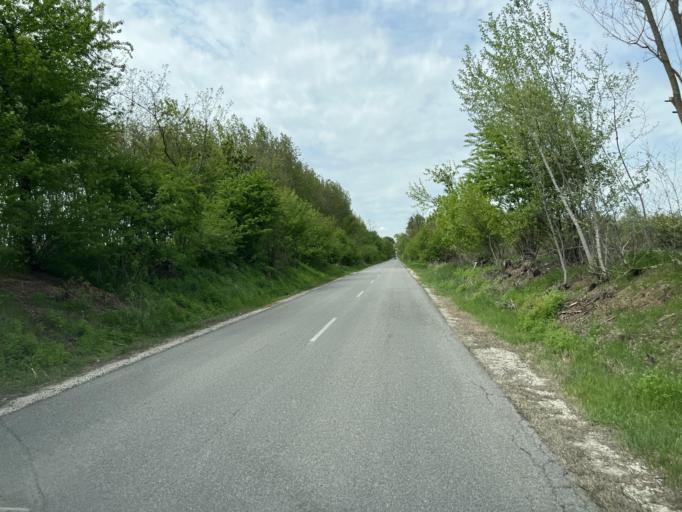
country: HU
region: Pest
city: Csemo
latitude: 47.1463
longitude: 19.6275
